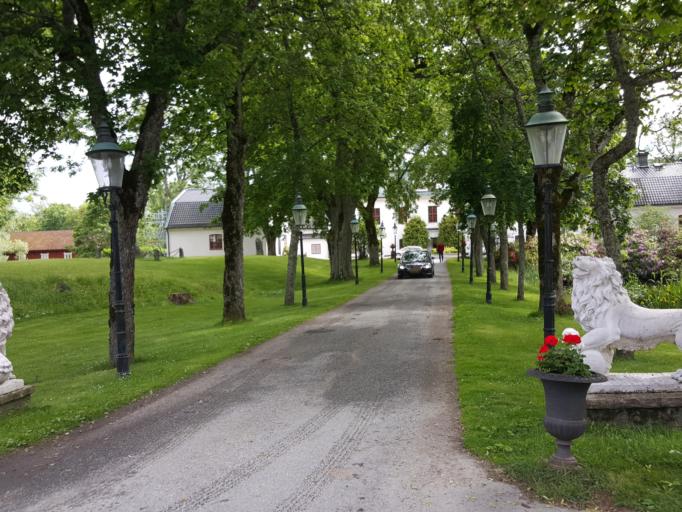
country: SE
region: Stockholm
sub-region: Nynashamns Kommun
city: Osmo
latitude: 59.0403
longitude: 18.0144
